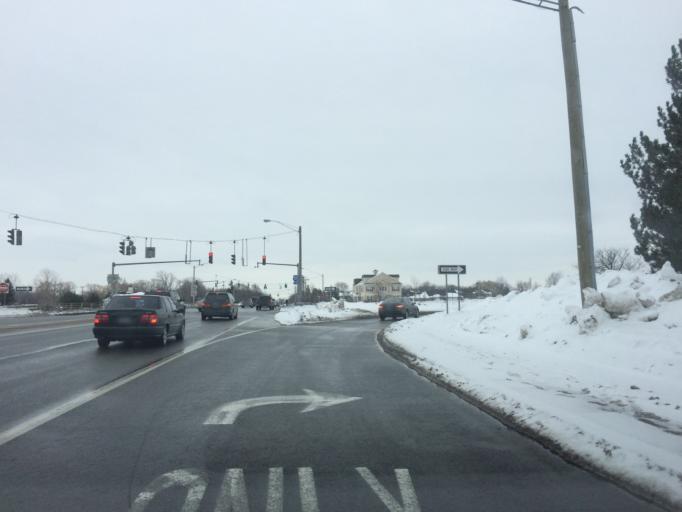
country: US
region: New York
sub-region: Monroe County
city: Rochester
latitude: 43.0851
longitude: -77.6084
